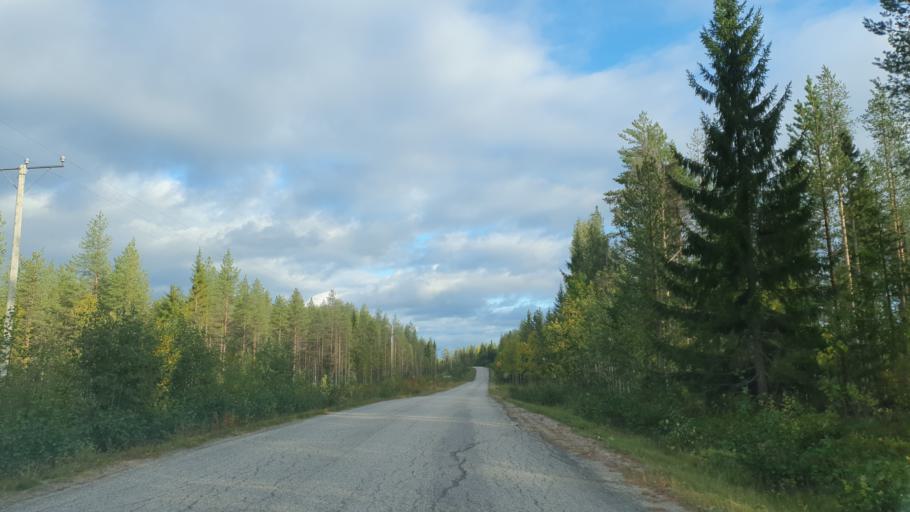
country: FI
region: Kainuu
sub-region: Kehys-Kainuu
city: Kuhmo
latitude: 63.9246
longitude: 30.0375
